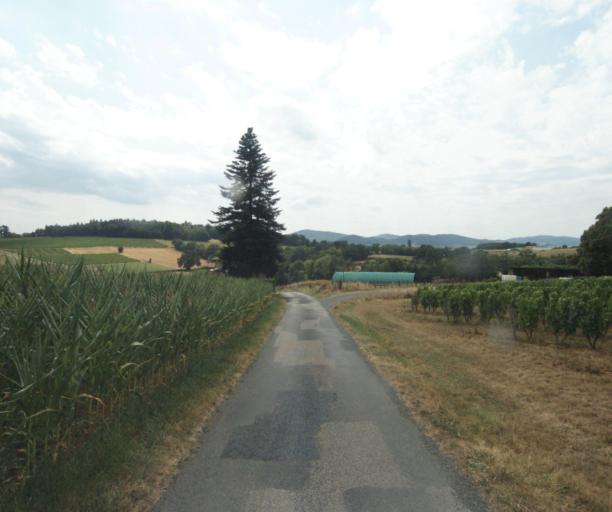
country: FR
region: Rhone-Alpes
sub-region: Departement du Rhone
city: Bully
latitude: 45.8627
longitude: 4.5882
